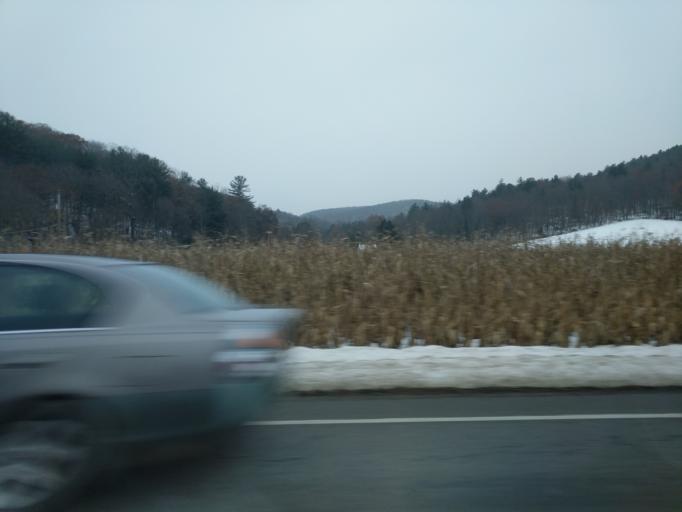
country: US
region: Pennsylvania
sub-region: Tioga County
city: Wellsboro
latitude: 41.7956
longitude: -77.3032
